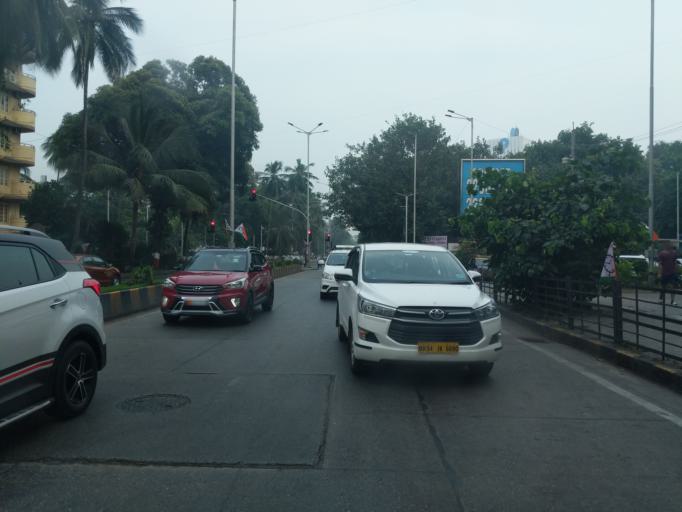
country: IN
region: Maharashtra
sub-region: Raigarh
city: Uran
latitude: 18.9291
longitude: 72.8226
